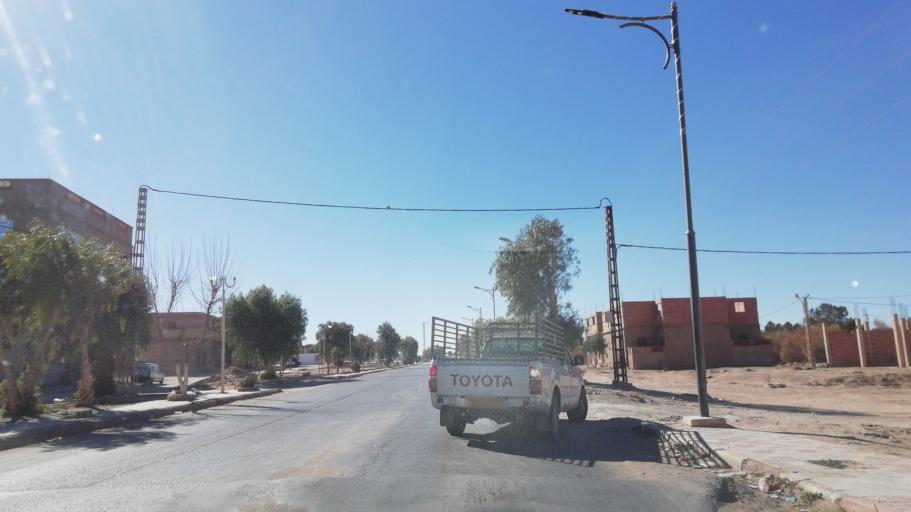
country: DZ
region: Saida
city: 'Ain el Hadjar
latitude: 34.0402
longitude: 0.0813
